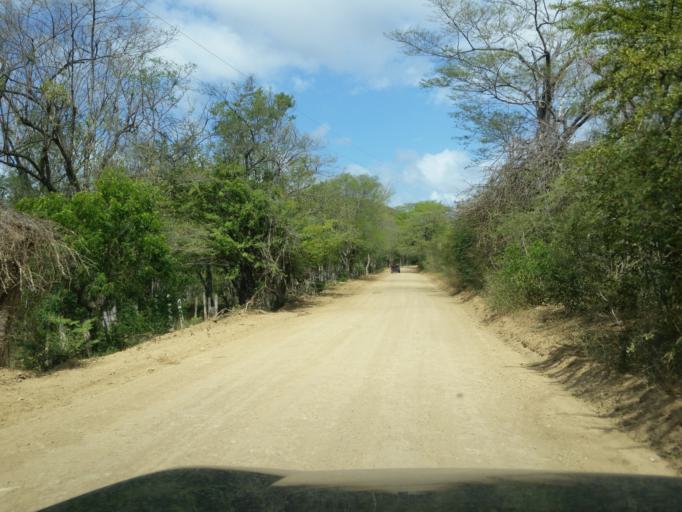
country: NI
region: Rivas
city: San Juan del Sur
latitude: 11.1293
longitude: -85.7802
